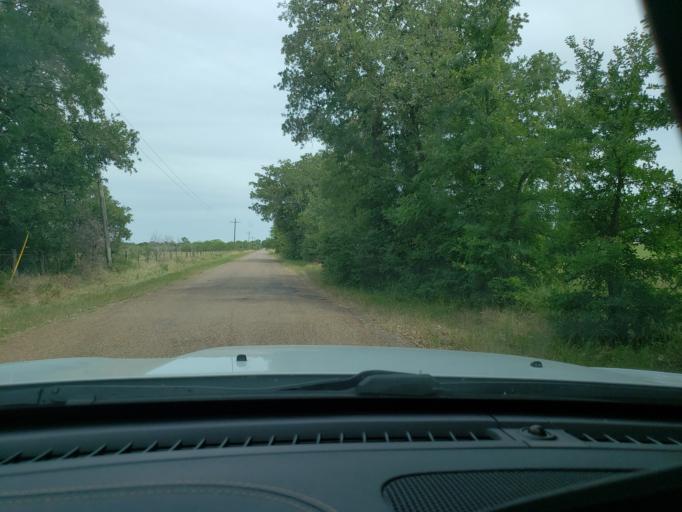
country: US
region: Texas
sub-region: Burleson County
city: Somerville
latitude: 30.3574
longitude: -96.5505
